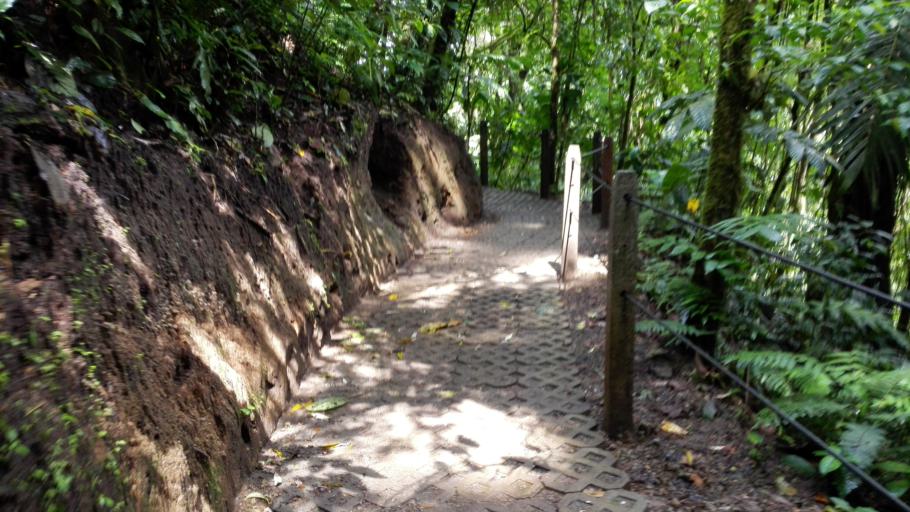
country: CR
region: Alajuela
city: La Fortuna
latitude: 10.4942
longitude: -84.7529
